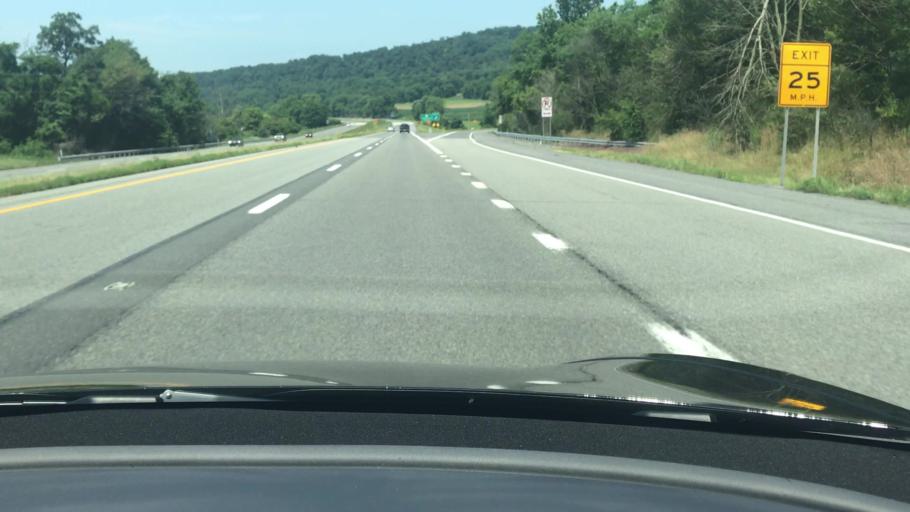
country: US
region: Pennsylvania
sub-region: Perry County
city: Newport
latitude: 40.5675
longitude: -77.1988
